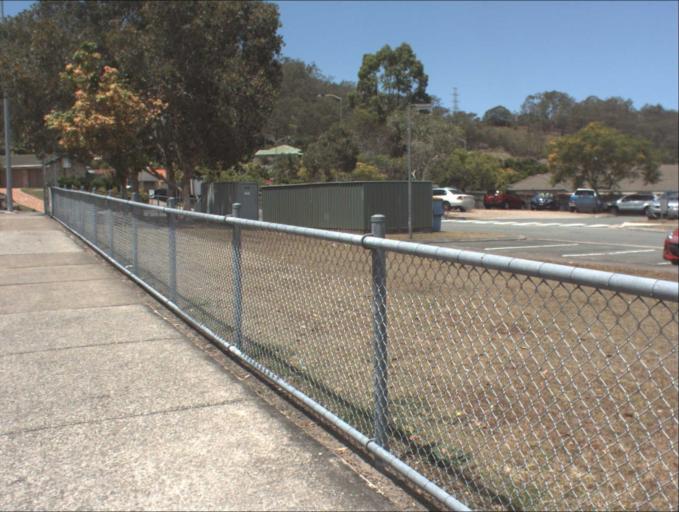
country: AU
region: Queensland
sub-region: Logan
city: Windaroo
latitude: -27.7322
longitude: 153.1962
